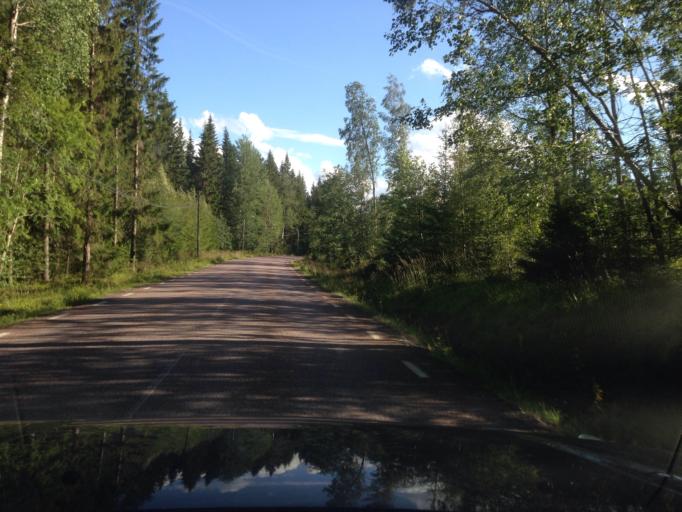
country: SE
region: Dalarna
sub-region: Ludvika Kommun
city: Grangesberg
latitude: 60.1697
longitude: 14.9769
